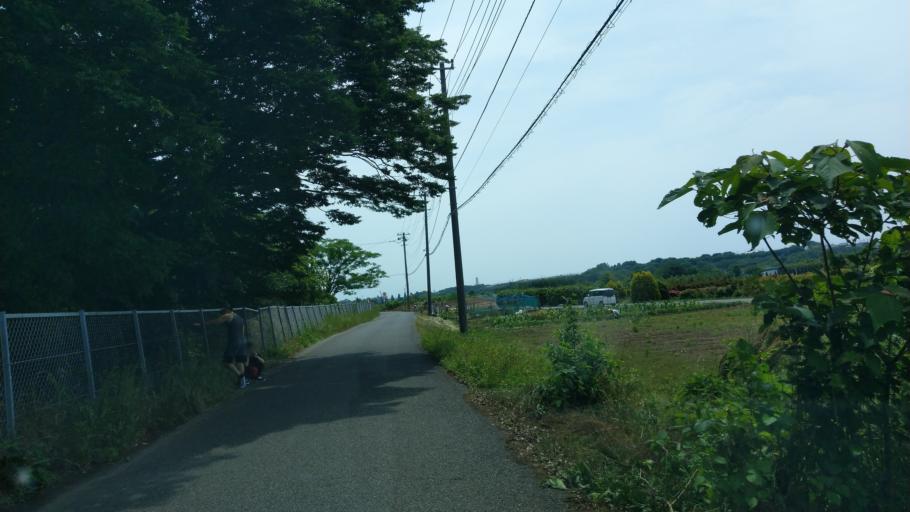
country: JP
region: Saitama
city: Saitama
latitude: 35.8967
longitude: 139.6820
